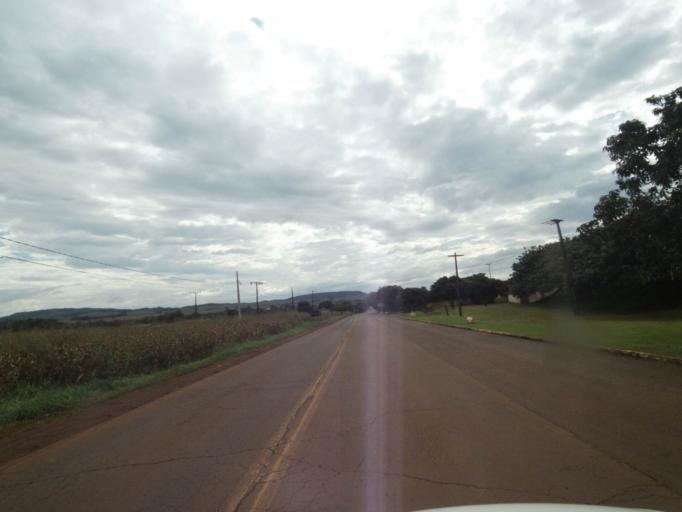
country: BR
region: Parana
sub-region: Marechal Candido Rondon
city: Marechal Candido Rondon
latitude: -24.7868
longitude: -54.2328
